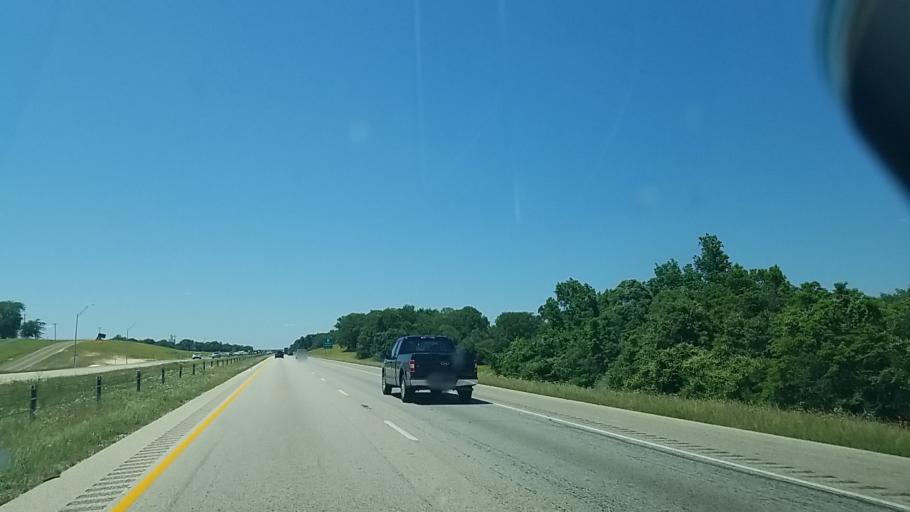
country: US
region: Texas
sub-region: Leon County
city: Buffalo
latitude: 31.4334
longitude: -96.0601
